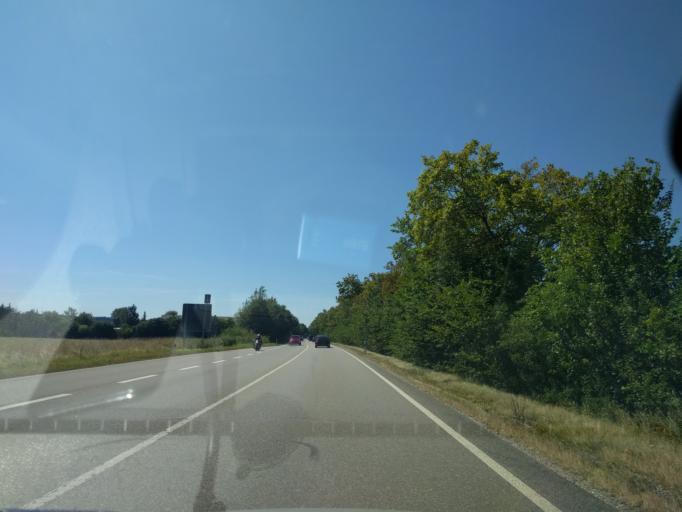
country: DE
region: Bavaria
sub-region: Upper Bavaria
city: Emmering
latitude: 48.1996
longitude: 11.2980
